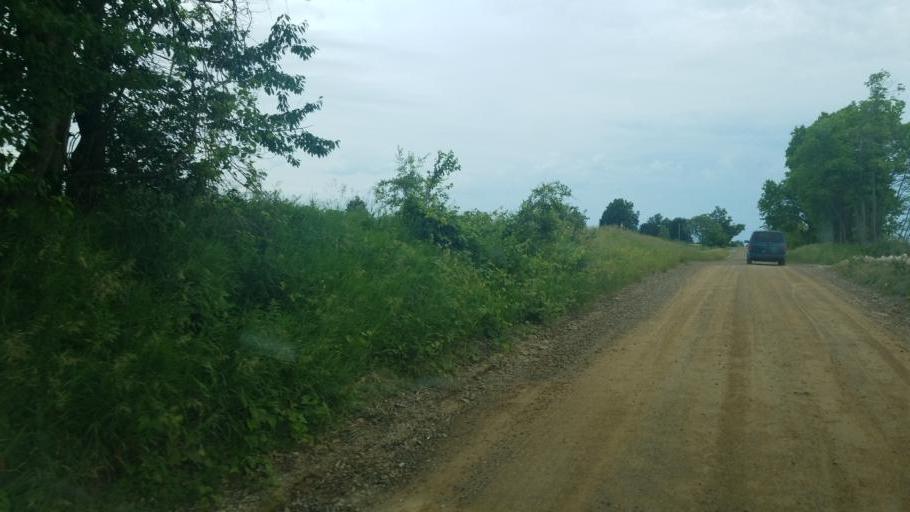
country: US
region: Michigan
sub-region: Barry County
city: Nashville
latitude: 42.6230
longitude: -84.9756
